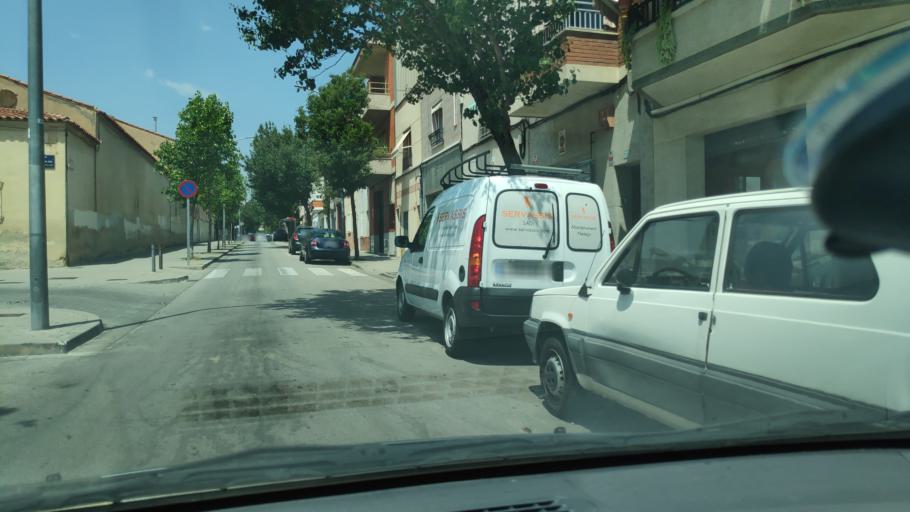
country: ES
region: Catalonia
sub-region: Provincia de Barcelona
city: Terrassa
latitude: 41.5644
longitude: 2.0305
